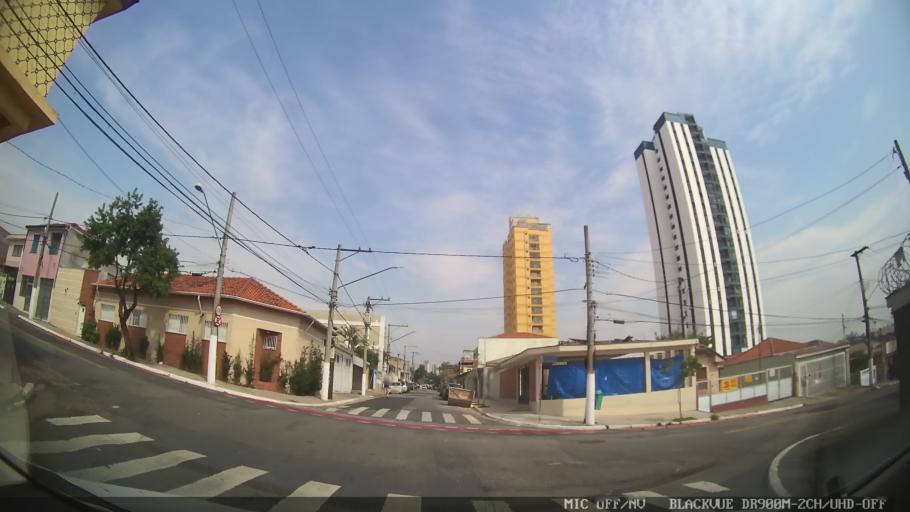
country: BR
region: Sao Paulo
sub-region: Sao Caetano Do Sul
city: Sao Caetano do Sul
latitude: -23.6105
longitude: -46.6035
